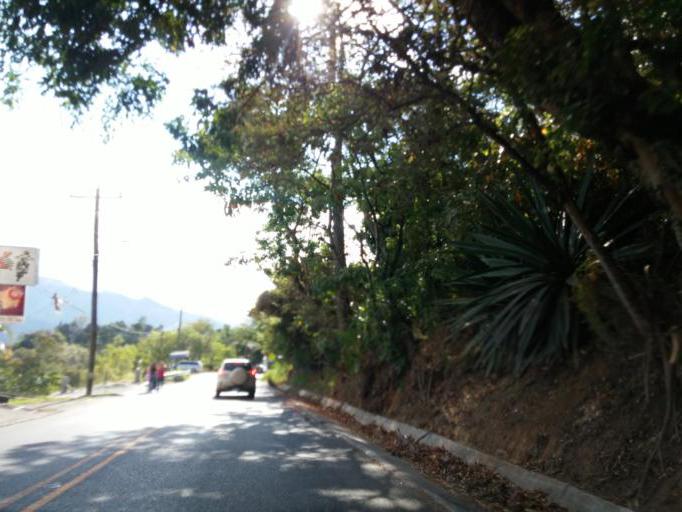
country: CR
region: San Jose
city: San Ignacio
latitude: 9.7971
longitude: -84.1270
